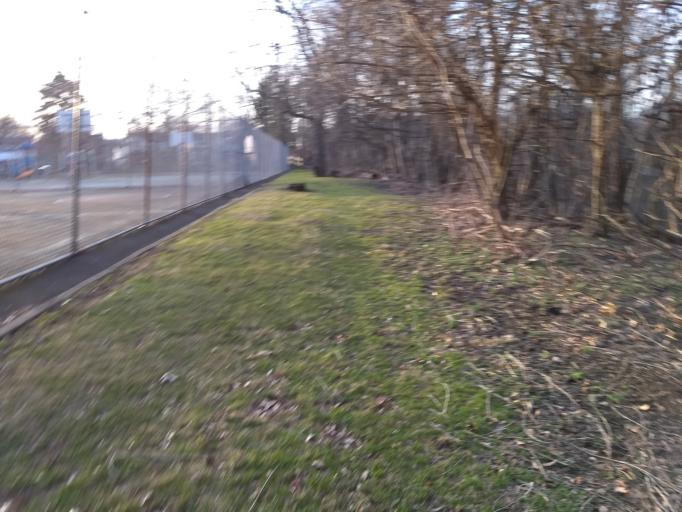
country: US
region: Pennsylvania
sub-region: Allegheny County
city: Green Tree
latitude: 40.4222
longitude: -80.0234
